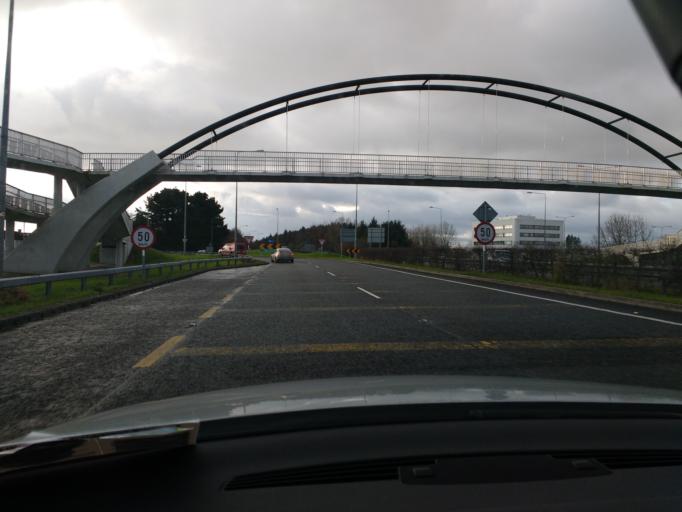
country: IE
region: Munster
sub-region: An Clar
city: Shannon
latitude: 52.7038
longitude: -8.8929
